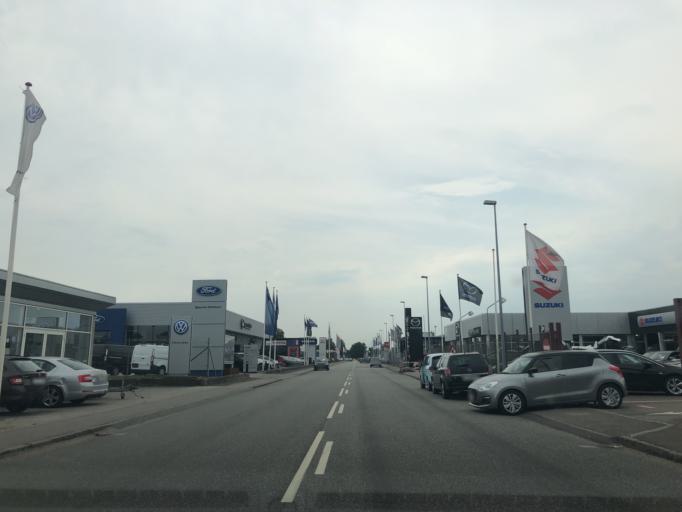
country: DK
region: Zealand
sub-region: Koge Kommune
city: Koge
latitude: 55.4754
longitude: 12.1849
